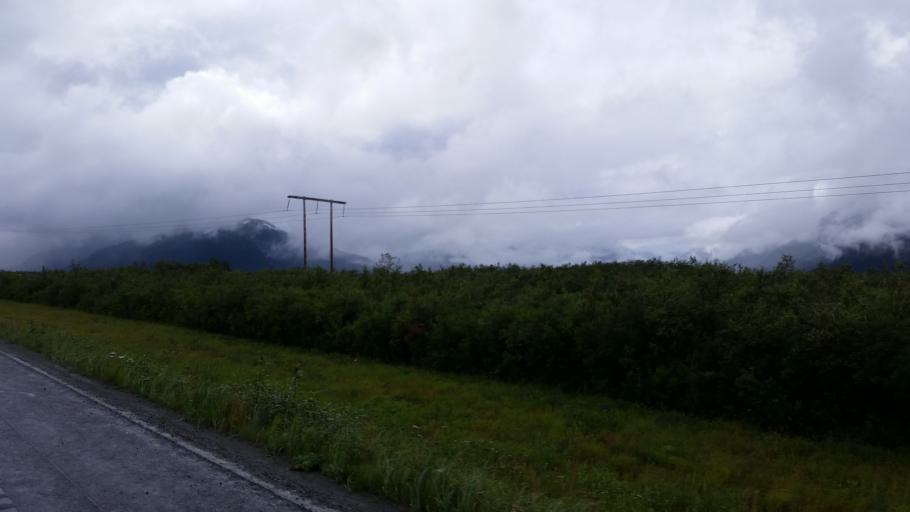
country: US
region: Alaska
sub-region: Anchorage Municipality
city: Girdwood
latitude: 60.8489
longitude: -148.9958
